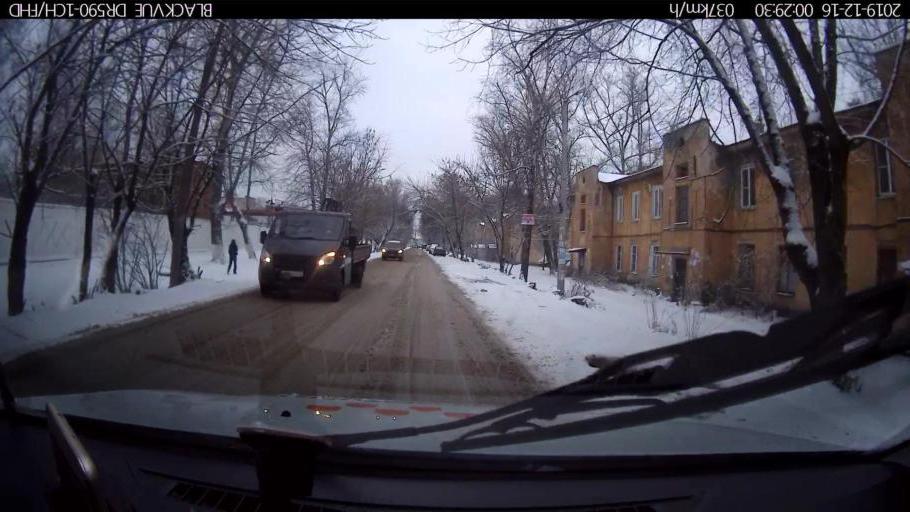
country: RU
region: Nizjnij Novgorod
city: Nizhniy Novgorod
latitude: 56.3122
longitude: 43.8903
